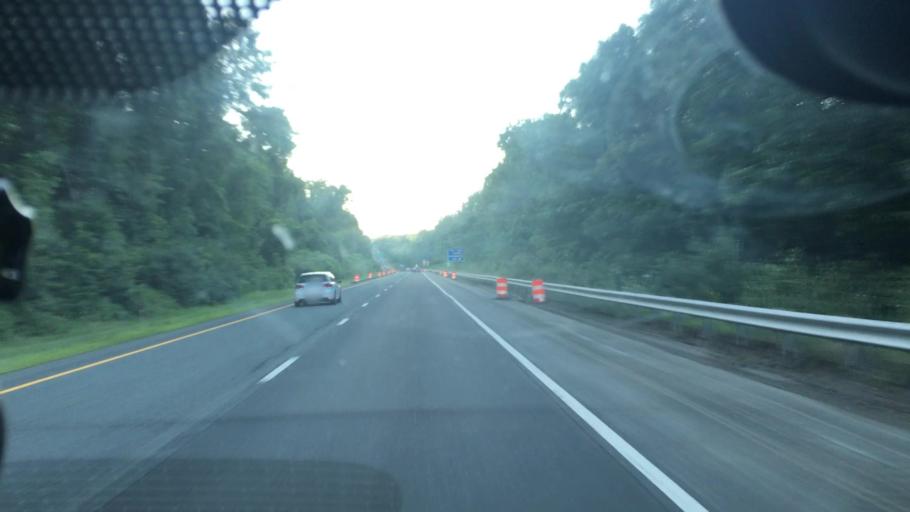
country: US
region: Massachusetts
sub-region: Franklin County
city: Greenfield
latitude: 42.5576
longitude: -72.6202
